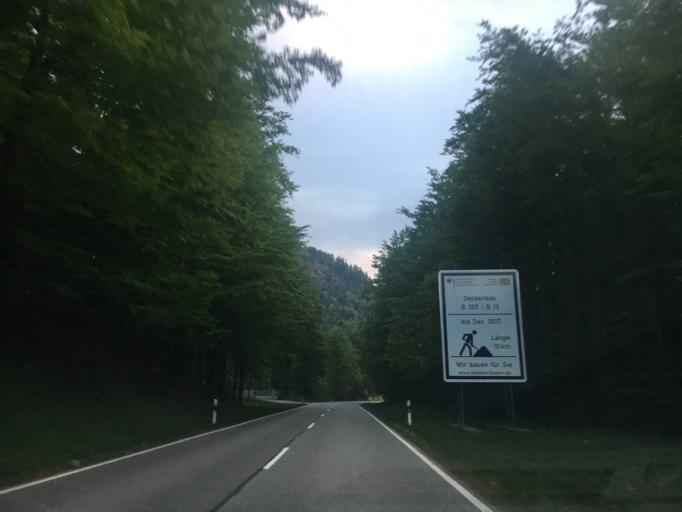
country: DE
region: Bavaria
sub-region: Upper Bavaria
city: Lenggries
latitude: 47.5915
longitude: 11.5530
